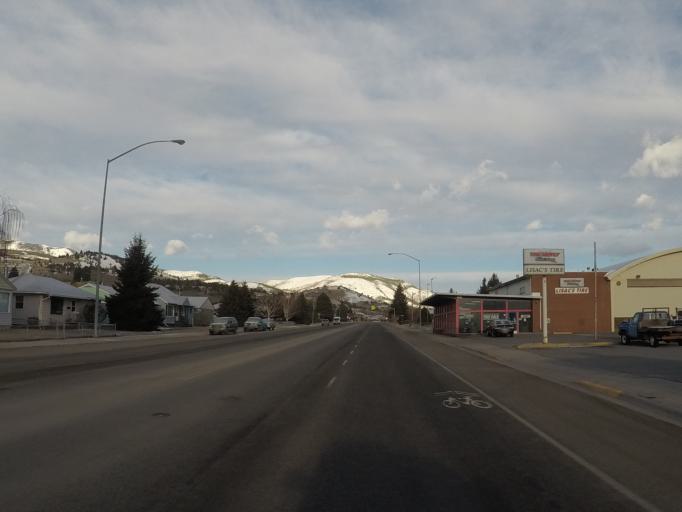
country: US
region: Montana
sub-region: Deer Lodge County
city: Anaconda
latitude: 46.1318
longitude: -112.9672
